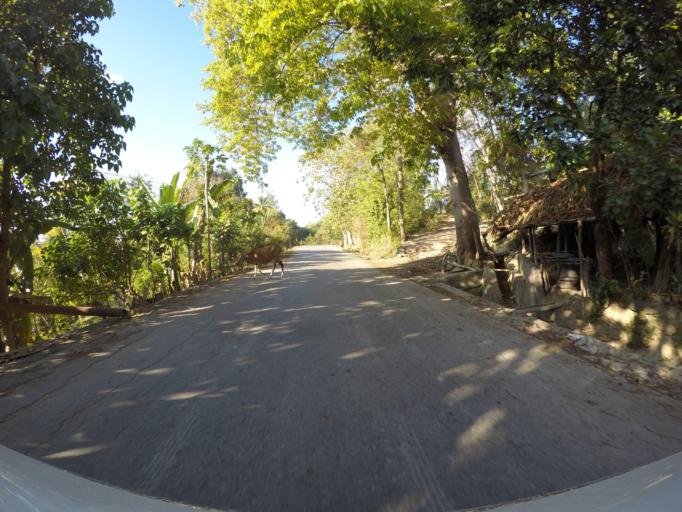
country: TL
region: Viqueque
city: Viqueque
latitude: -8.8700
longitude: 126.3618
